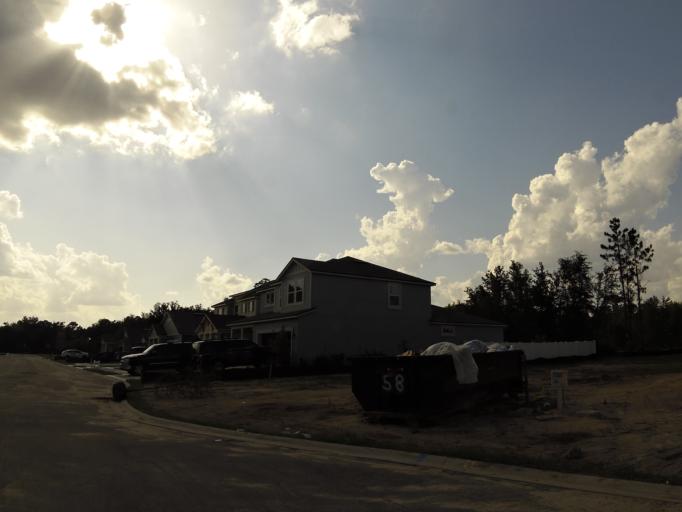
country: US
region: Florida
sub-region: Clay County
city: Green Cove Springs
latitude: 30.0240
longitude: -81.6286
